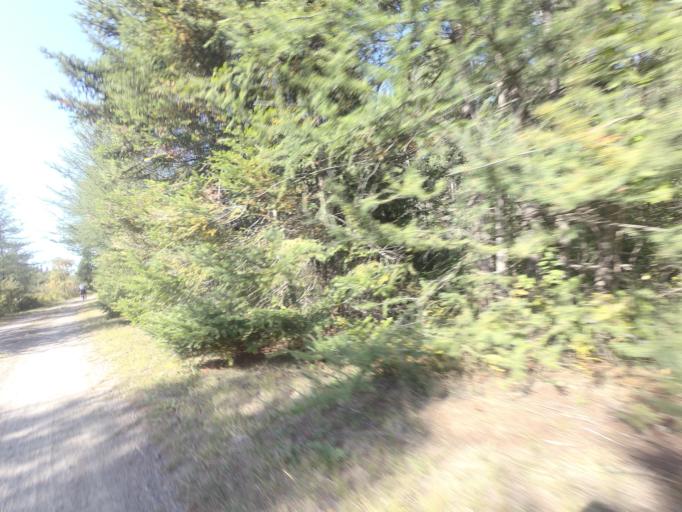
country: CA
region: Quebec
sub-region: Laurentides
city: Sainte-Agathe-des-Monts
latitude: 46.1039
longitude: -74.3931
